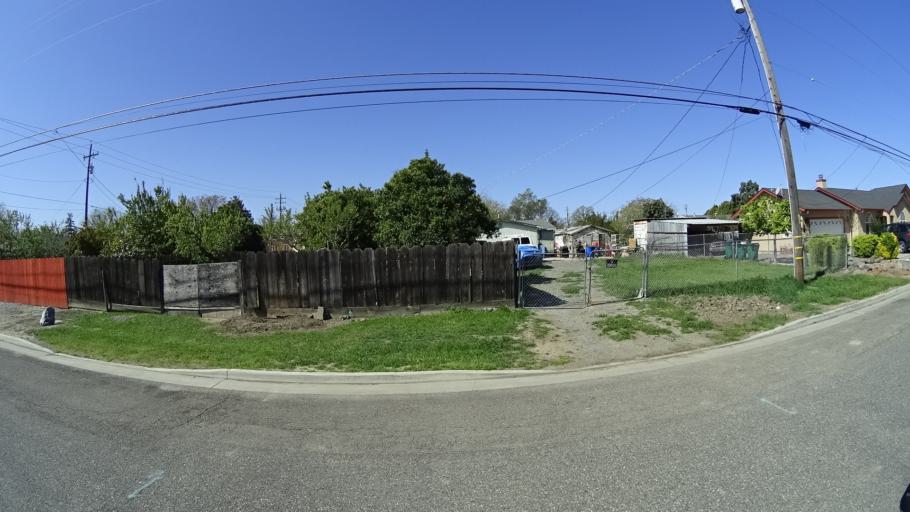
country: US
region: California
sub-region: Glenn County
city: Hamilton City
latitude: 39.7451
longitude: -122.0128
